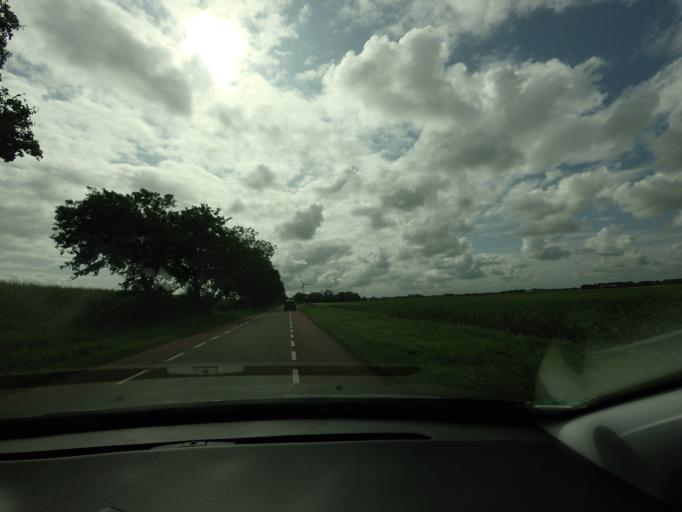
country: NL
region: North Holland
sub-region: Gemeente Medemblik
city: Medemblik
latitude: 52.8018
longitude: 5.1060
